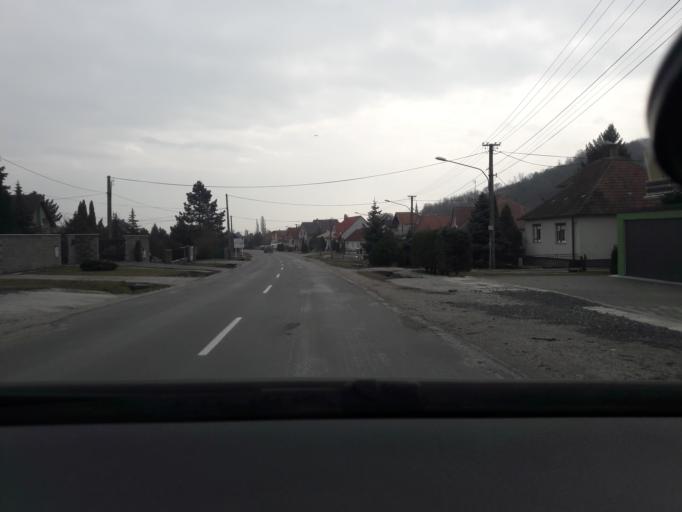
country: SK
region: Trnavsky
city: Smolenice
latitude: 48.4731
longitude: 17.4340
